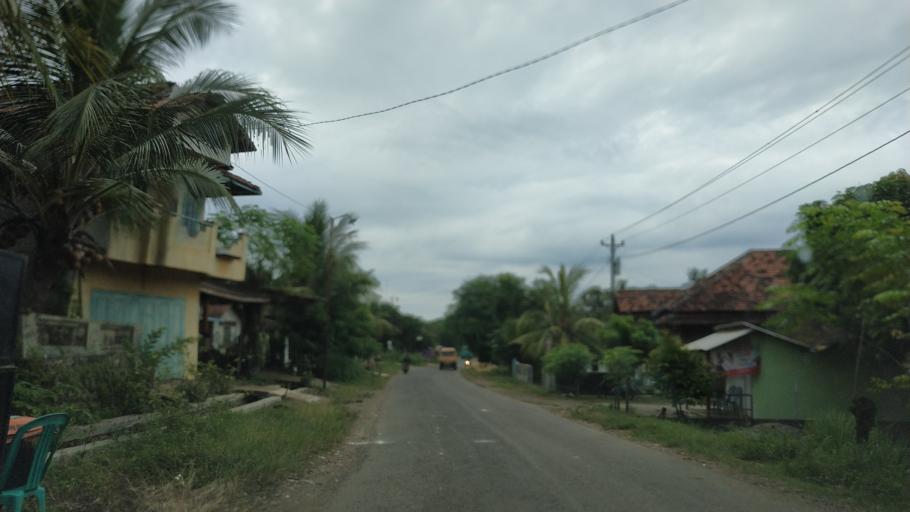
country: ID
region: Central Java
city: Krajan Tegalombo
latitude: -6.4446
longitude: 110.9845
